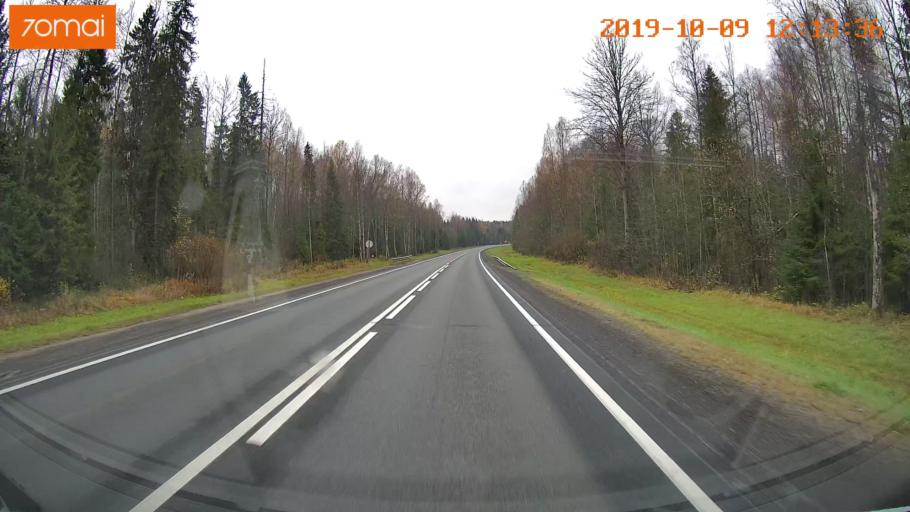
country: RU
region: Jaroslavl
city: Prechistoye
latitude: 58.5081
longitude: 40.3449
